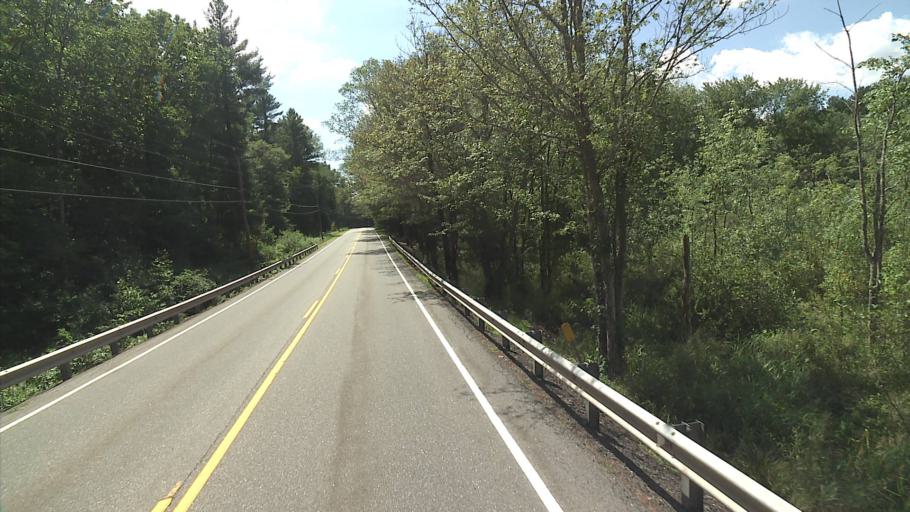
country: US
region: Connecticut
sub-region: Windham County
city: South Woodstock
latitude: 41.9604
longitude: -72.0790
